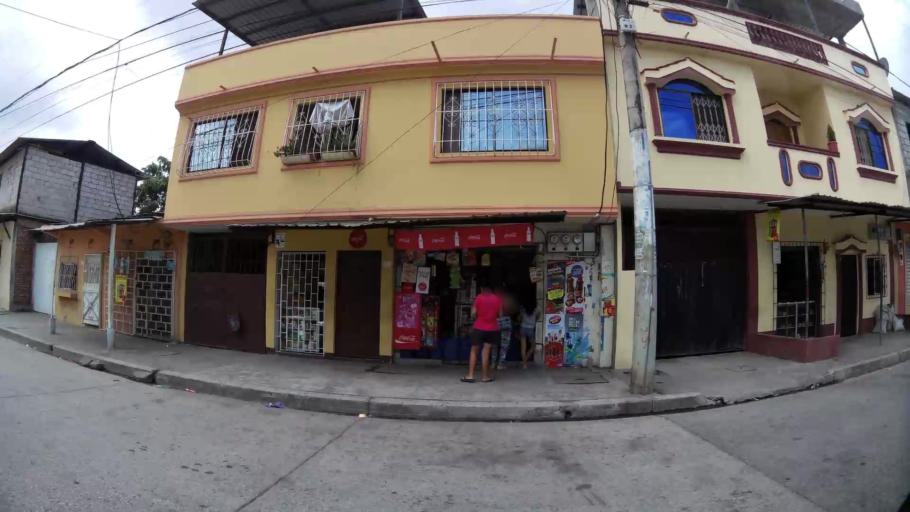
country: EC
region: Guayas
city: Guayaquil
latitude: -2.2375
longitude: -79.9194
